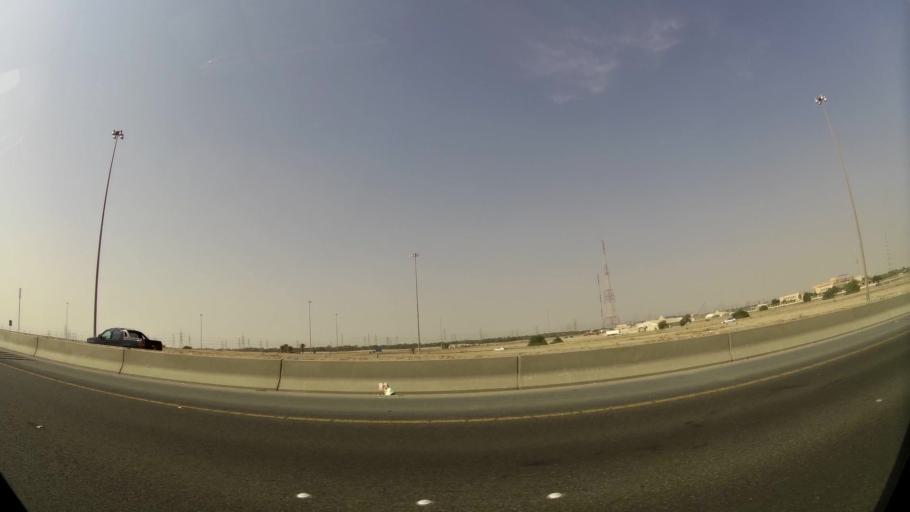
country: KW
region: Al Ahmadi
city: Al Fahahil
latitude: 29.0760
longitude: 48.1126
